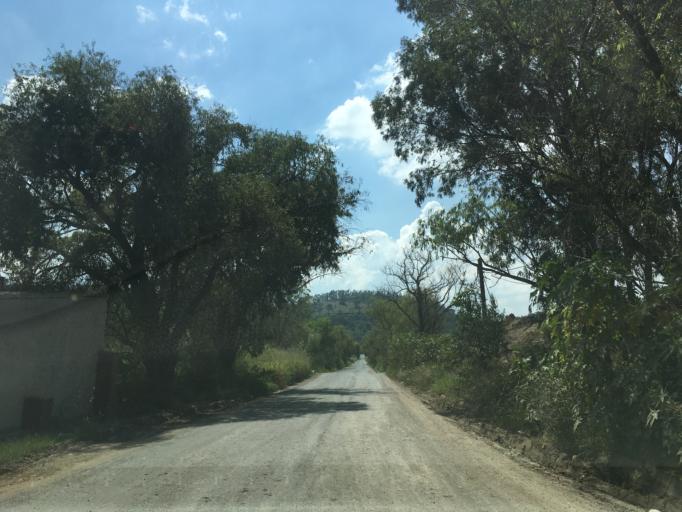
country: MX
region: Michoacan
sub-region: Morelia
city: La Mintzita (Piedra Dura)
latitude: 19.6478
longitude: -101.2650
